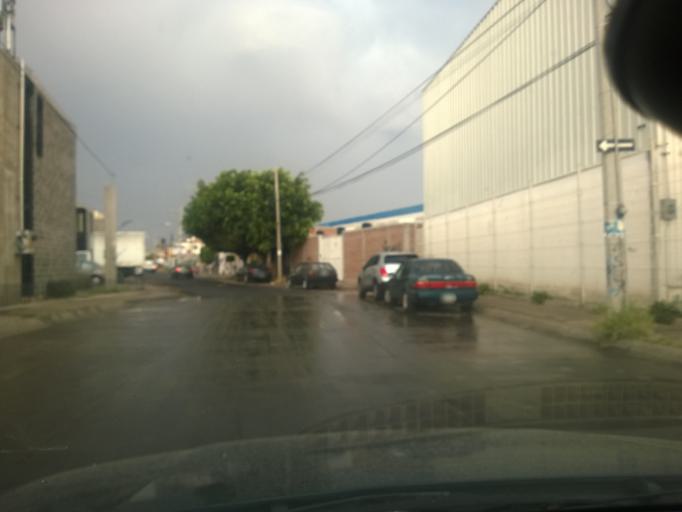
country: MX
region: Guanajuato
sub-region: Leon
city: Fraccionamiento Paraiso Real
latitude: 21.0833
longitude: -101.6208
